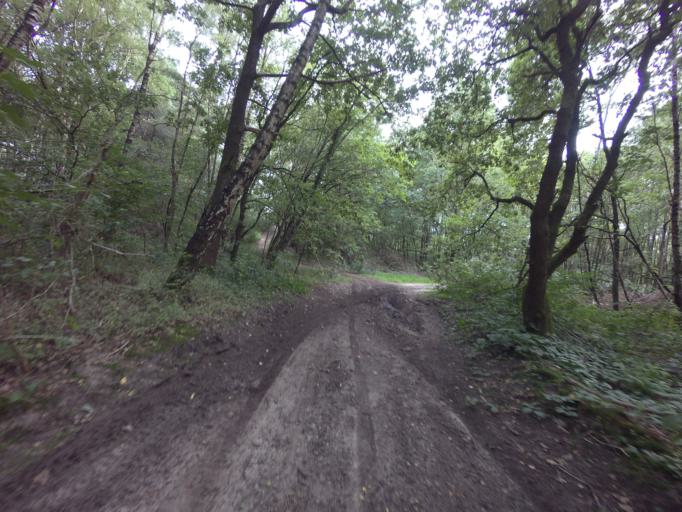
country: DE
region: Lower Saxony
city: Getelo
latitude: 52.4605
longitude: 6.8546
